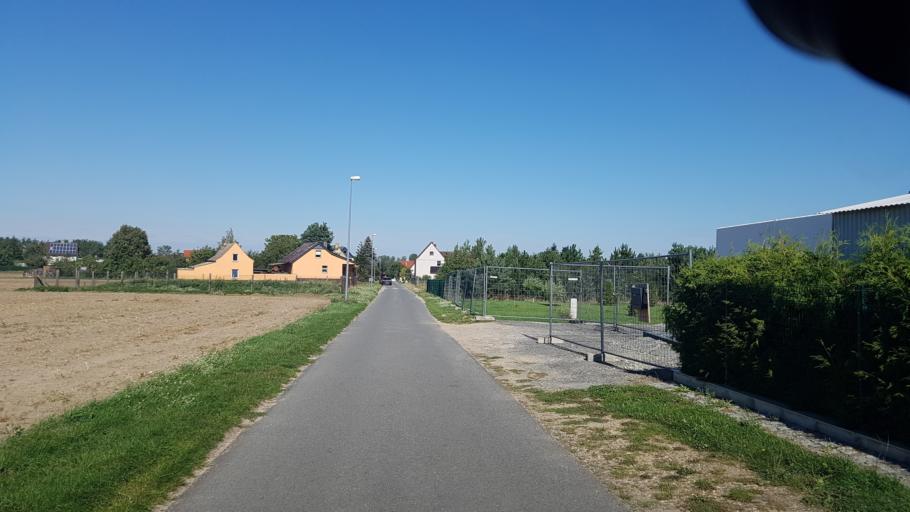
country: DE
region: Brandenburg
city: Hirschfeld
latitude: 51.3903
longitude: 13.6134
